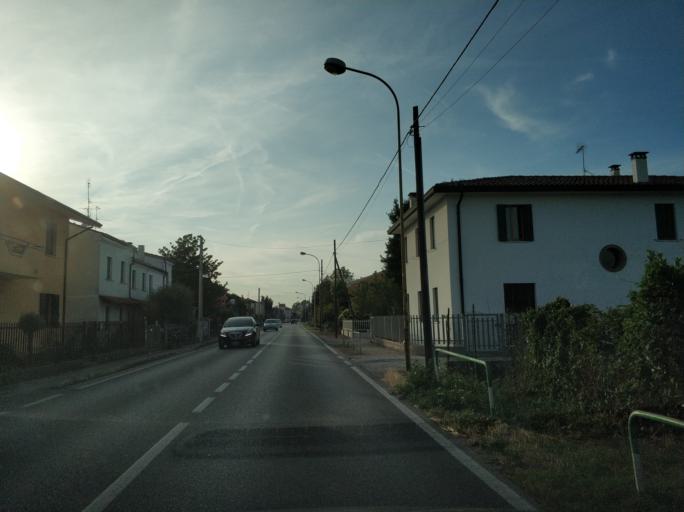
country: IT
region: Veneto
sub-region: Provincia di Padova
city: Este
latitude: 45.2172
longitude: 11.6672
